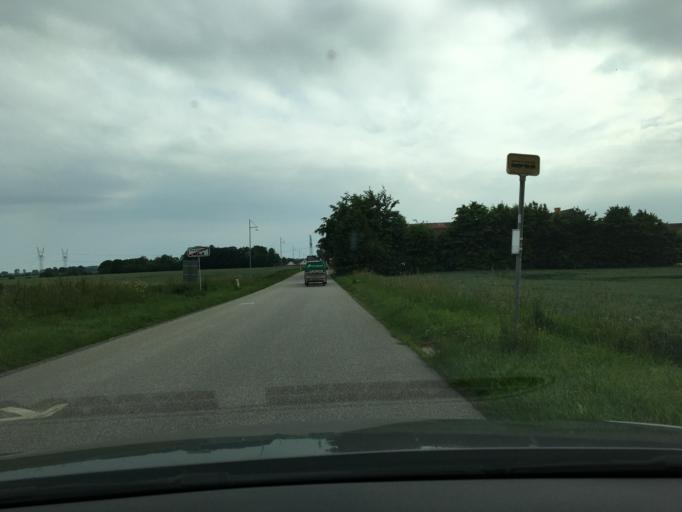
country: DK
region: South Denmark
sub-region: Middelfart Kommune
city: Norre Aby
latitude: 55.4740
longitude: 9.8085
